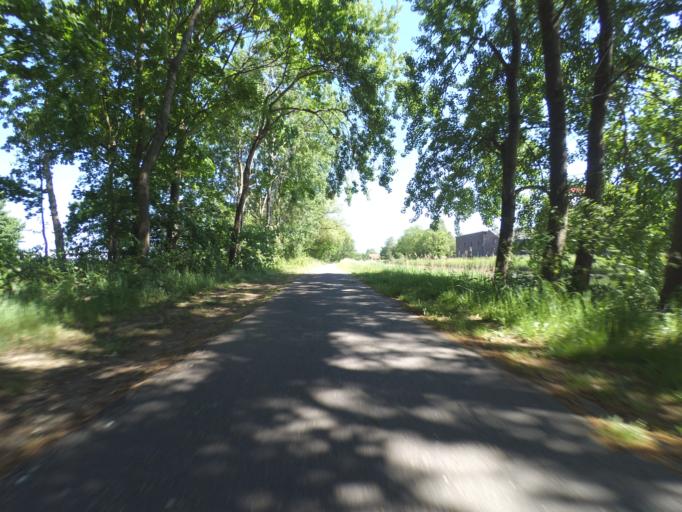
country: NL
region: Gelderland
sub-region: Gemeente Apeldoorn
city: Apeldoorn
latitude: 52.2404
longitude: 5.9756
